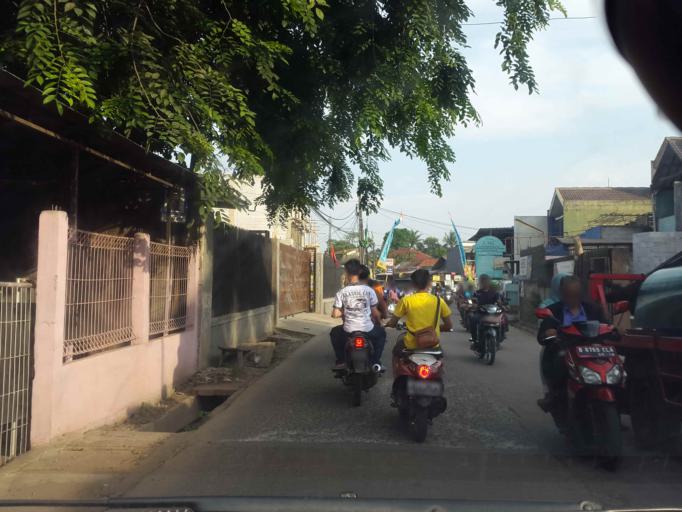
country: ID
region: West Java
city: Ciputat
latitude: -6.2439
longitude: 106.6922
